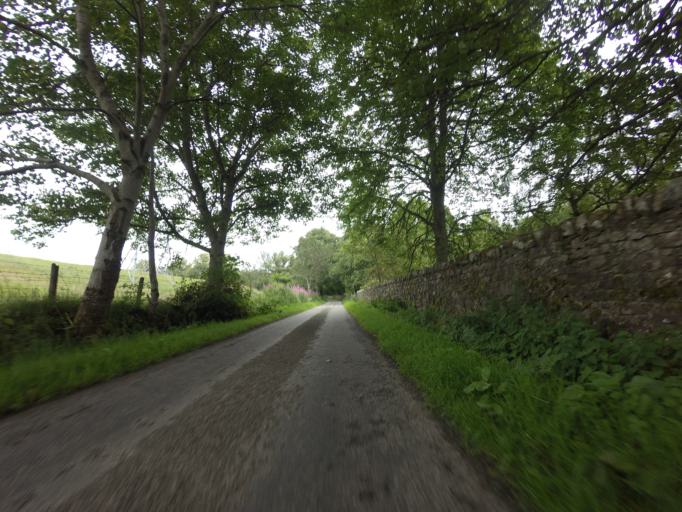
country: GB
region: Scotland
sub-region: Highland
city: Alness
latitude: 57.8917
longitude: -4.3760
